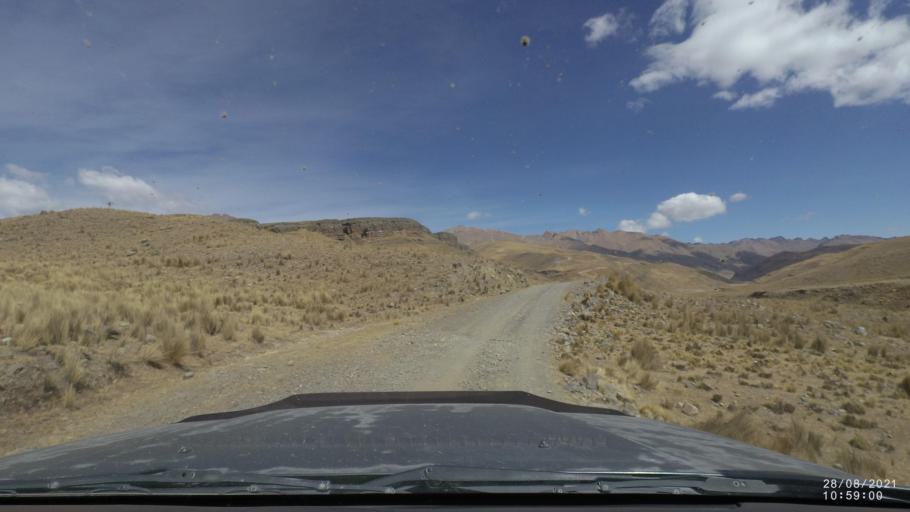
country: BO
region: Cochabamba
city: Cochabamba
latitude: -17.1830
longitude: -66.2551
